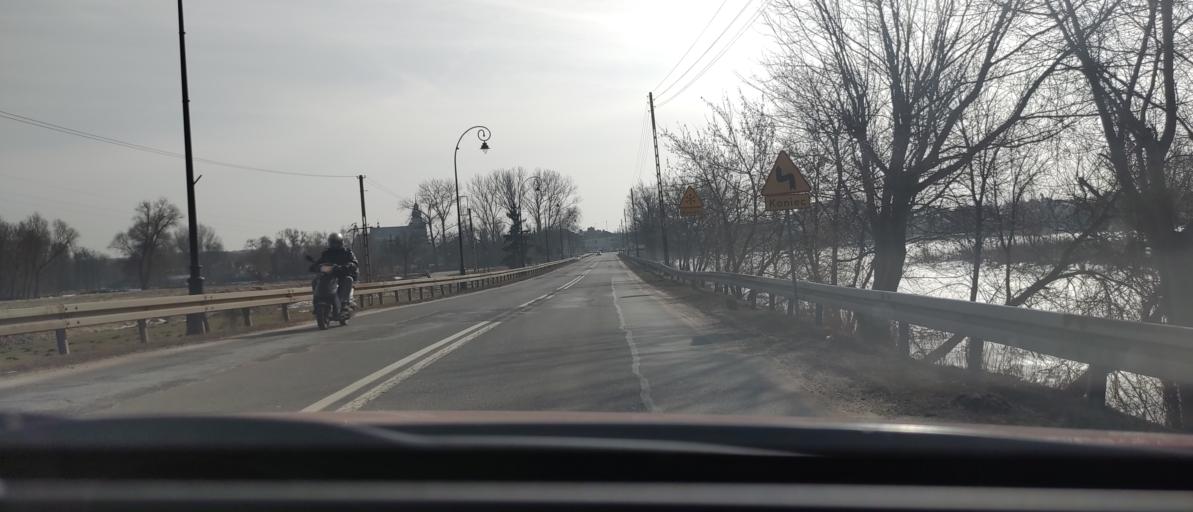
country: PL
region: Masovian Voivodeship
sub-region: Powiat bialobrzeski
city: Bialobrzegi
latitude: 51.6550
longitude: 20.9514
